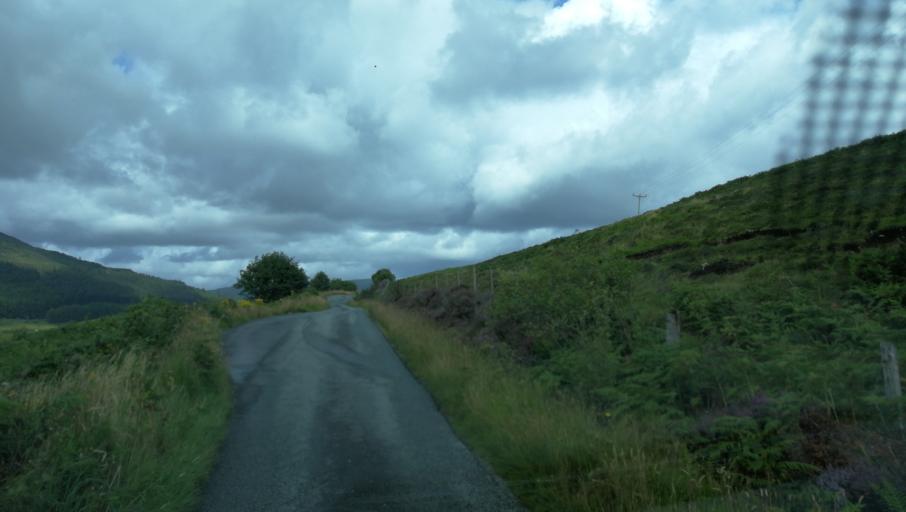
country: GB
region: Scotland
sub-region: Highland
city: Portree
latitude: 57.3833
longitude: -6.1946
